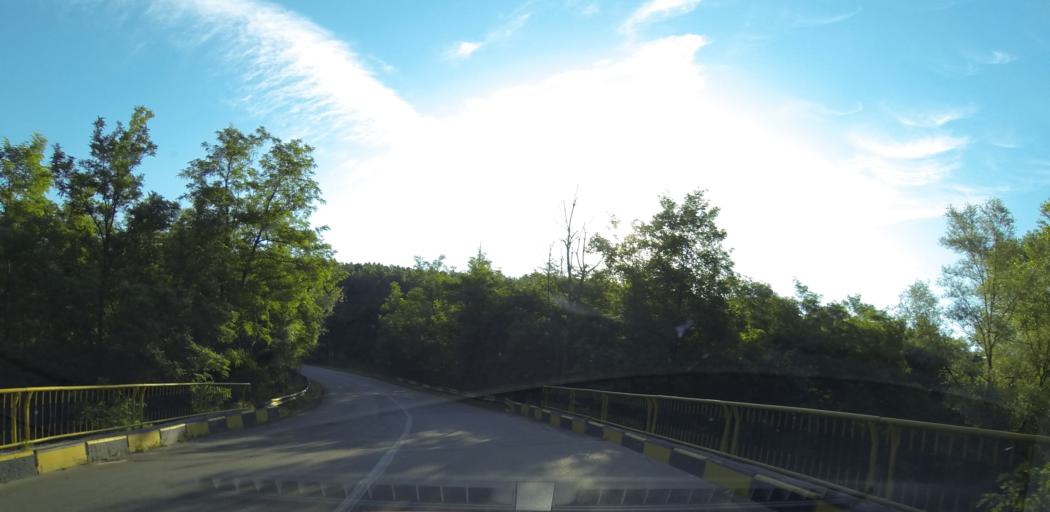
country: RO
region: Valcea
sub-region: Comuna Balcesti
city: Balcesti
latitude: 44.5889
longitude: 23.9215
